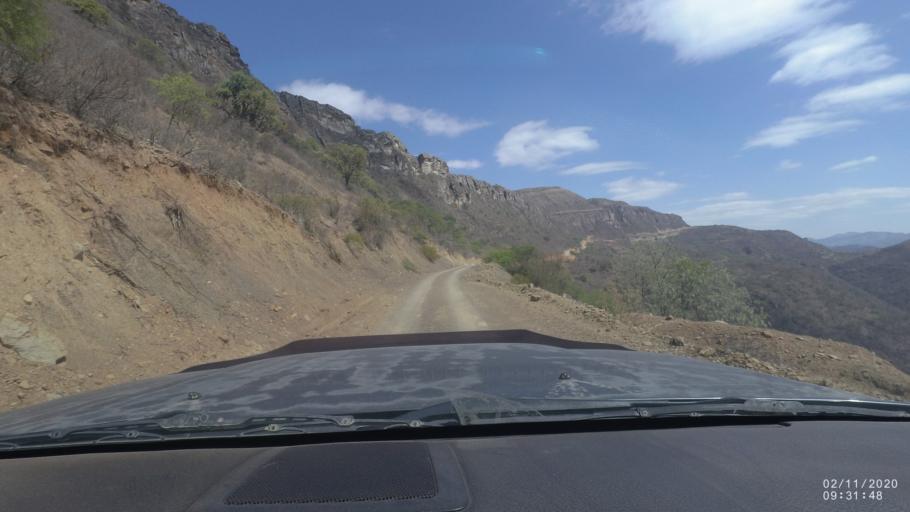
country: BO
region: Chuquisaca
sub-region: Provincia Zudanez
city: Mojocoya
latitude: -18.4255
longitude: -64.5848
